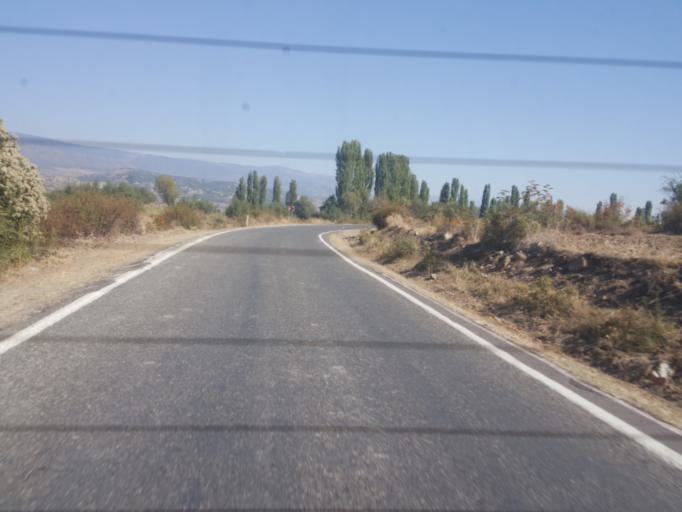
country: TR
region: Kastamonu
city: Tosya
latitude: 40.9936
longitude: 34.1278
